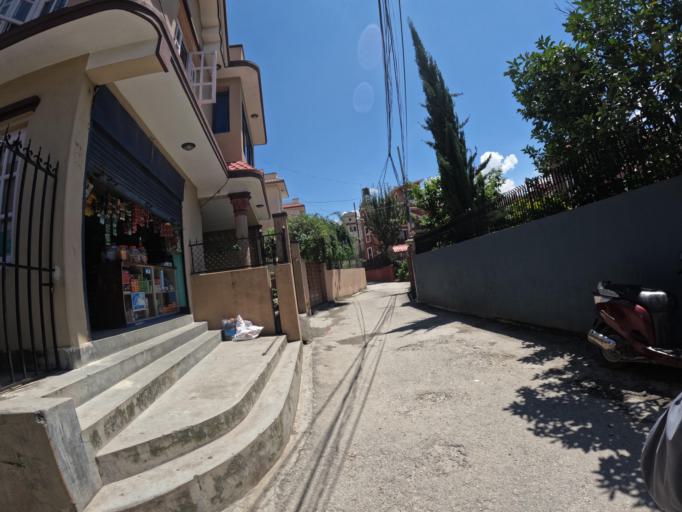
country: NP
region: Central Region
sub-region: Bagmati Zone
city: Kathmandu
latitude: 27.7499
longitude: 85.3267
